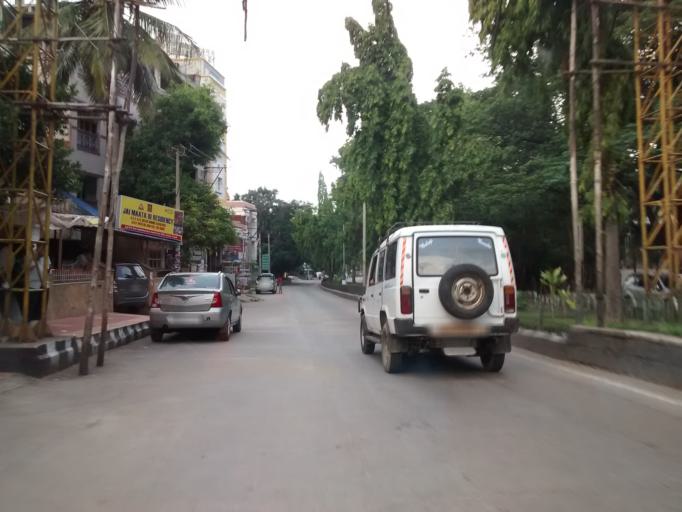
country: IN
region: Andhra Pradesh
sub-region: Chittoor
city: Akkarampalle
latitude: 13.6537
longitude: 79.4198
